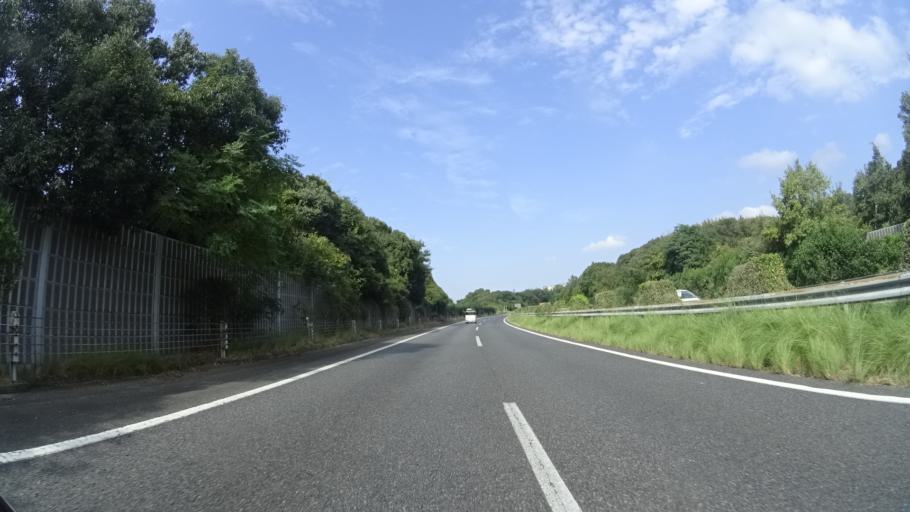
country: JP
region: Kumamoto
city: Matsubase
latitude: 32.6201
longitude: 130.7144
